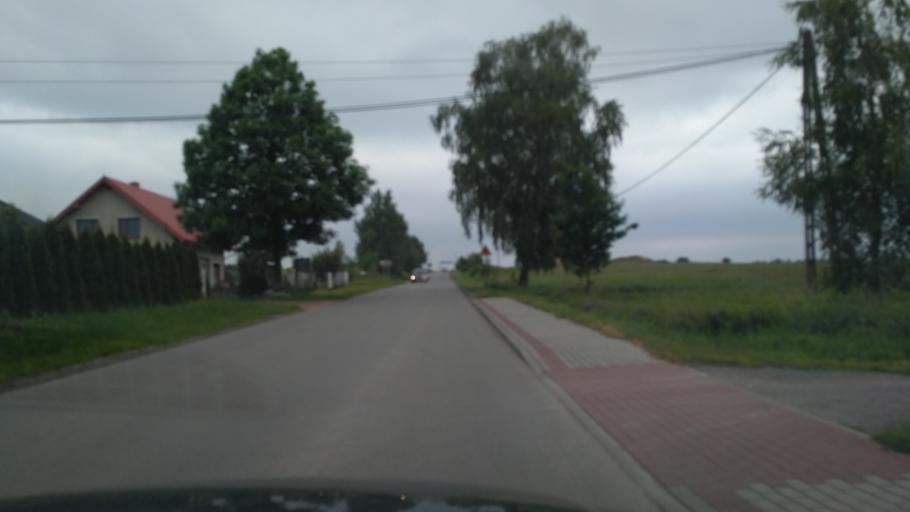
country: PL
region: Subcarpathian Voivodeship
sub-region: Powiat ropczycko-sedziszowski
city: Sedziszow Malopolski
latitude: 50.1007
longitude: 21.6673
